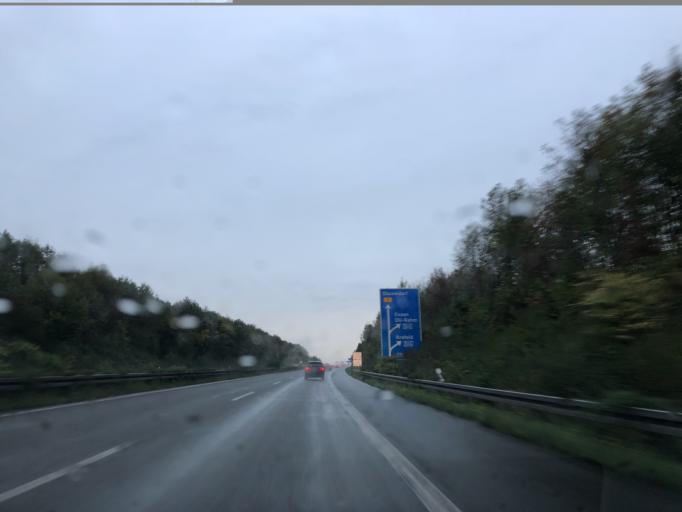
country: DE
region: North Rhine-Westphalia
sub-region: Regierungsbezirk Dusseldorf
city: Hochfeld
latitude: 51.3620
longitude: 6.7662
